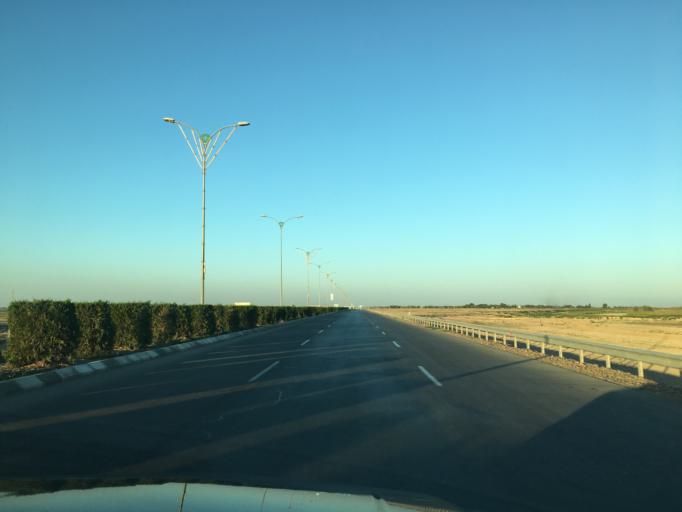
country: TM
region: Dasoguz
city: Dasoguz
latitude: 41.7791
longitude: 59.8519
